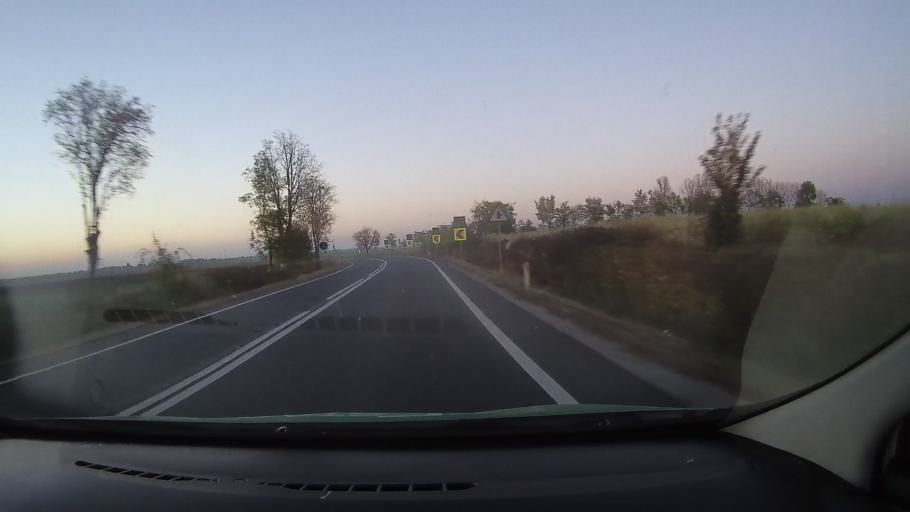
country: RO
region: Bihor
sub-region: Comuna Tarcea
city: Tarcea
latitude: 47.4794
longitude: 22.1633
